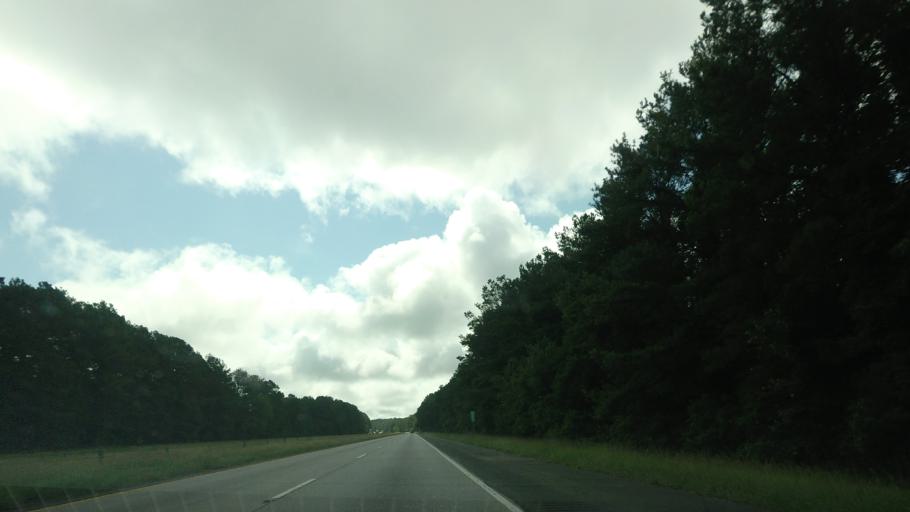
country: US
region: Georgia
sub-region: Twiggs County
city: Jeffersonville
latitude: 32.6429
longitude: -83.4068
